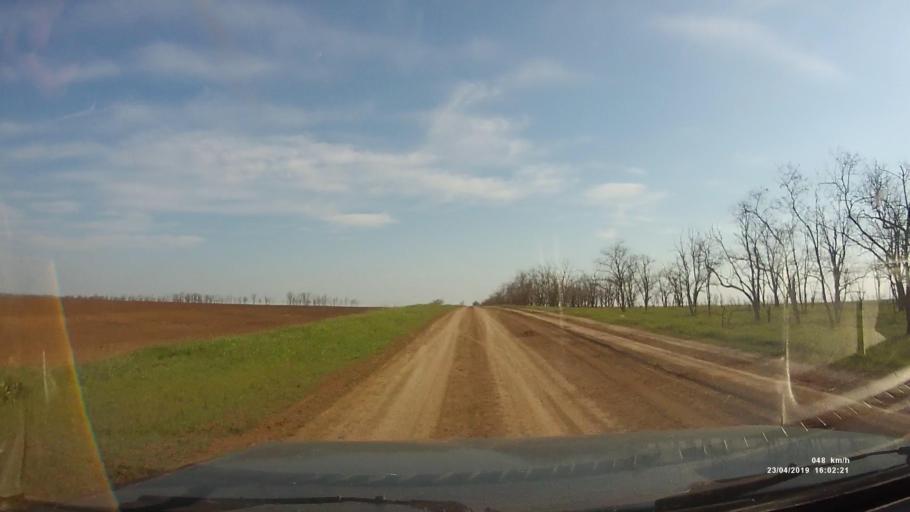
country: RU
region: Rostov
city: Remontnoye
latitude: 46.4950
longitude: 43.1070
